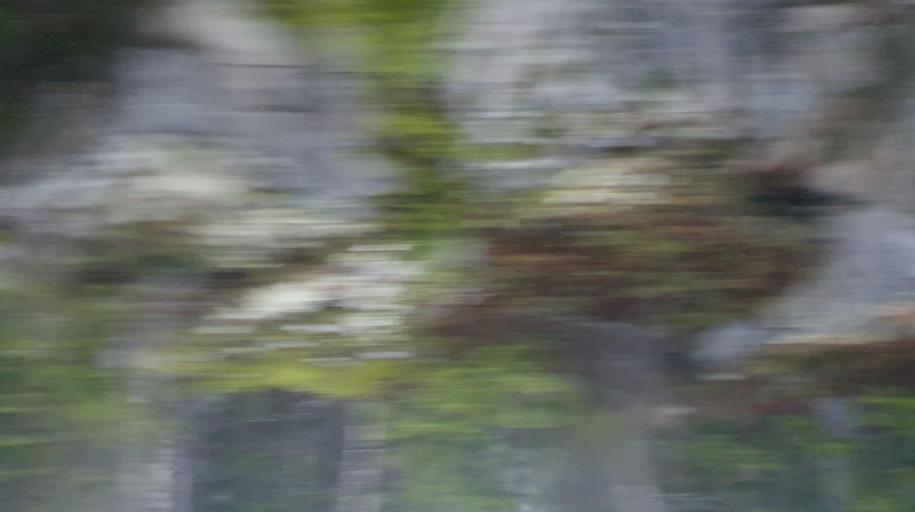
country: NO
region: Buskerud
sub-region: Krodsherad
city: Noresund
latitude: 60.2164
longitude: 9.5432
